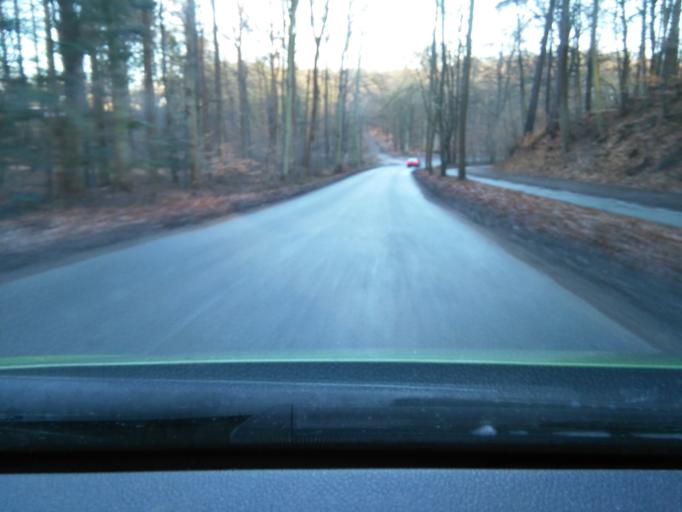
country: DK
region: Central Jutland
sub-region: Arhus Kommune
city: Arhus
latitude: 56.1138
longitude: 10.2246
